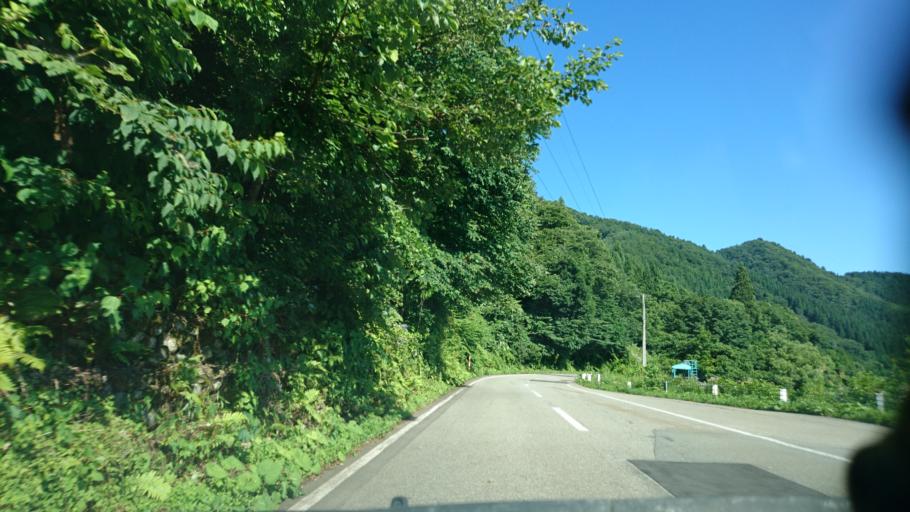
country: JP
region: Akita
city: Kakunodatemachi
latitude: 39.7163
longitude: 140.6311
